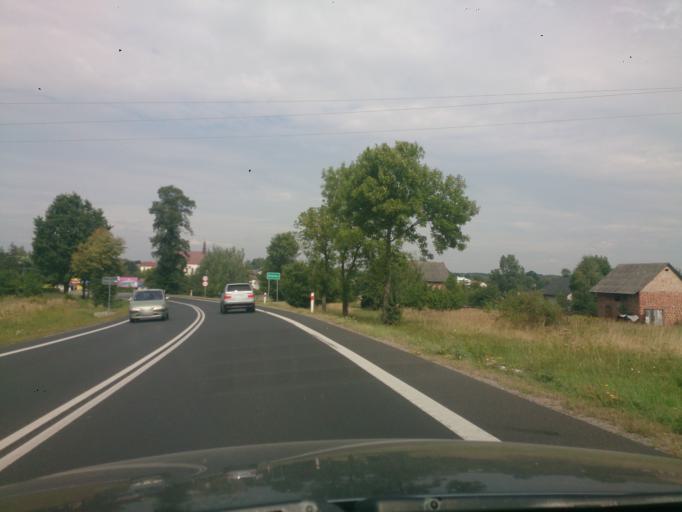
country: PL
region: Subcarpathian Voivodeship
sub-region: Powiat kolbuszowski
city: Dzikowiec
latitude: 50.1989
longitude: 21.8840
